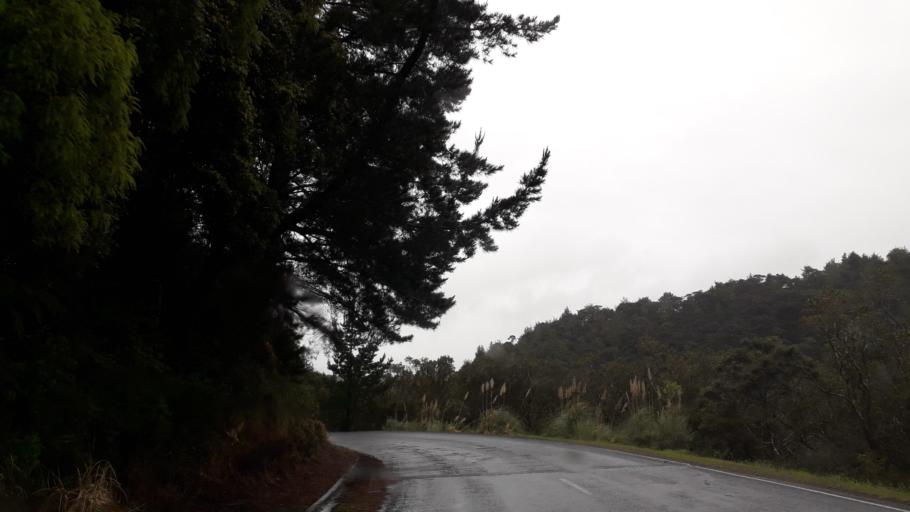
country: NZ
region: Northland
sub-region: Far North District
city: Kaitaia
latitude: -35.3637
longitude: 173.4724
